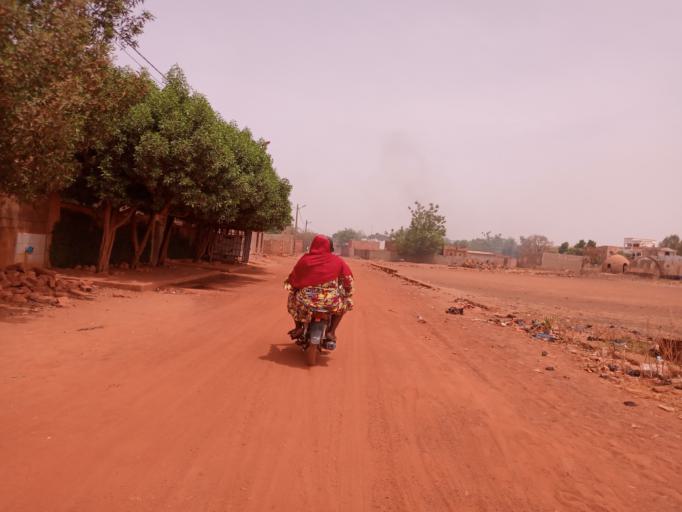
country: ML
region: Bamako
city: Bamako
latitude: 12.6743
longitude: -7.9099
